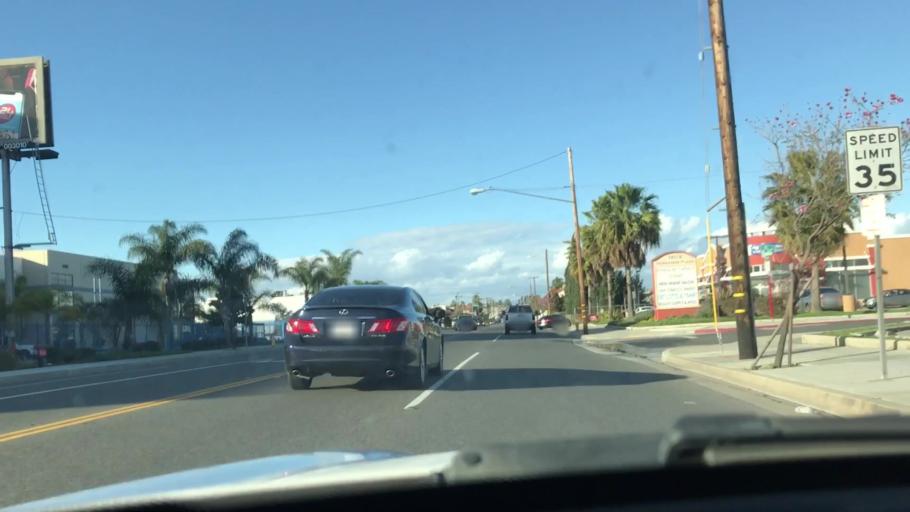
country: US
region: California
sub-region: Los Angeles County
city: Gardena
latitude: 33.9024
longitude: -118.3004
